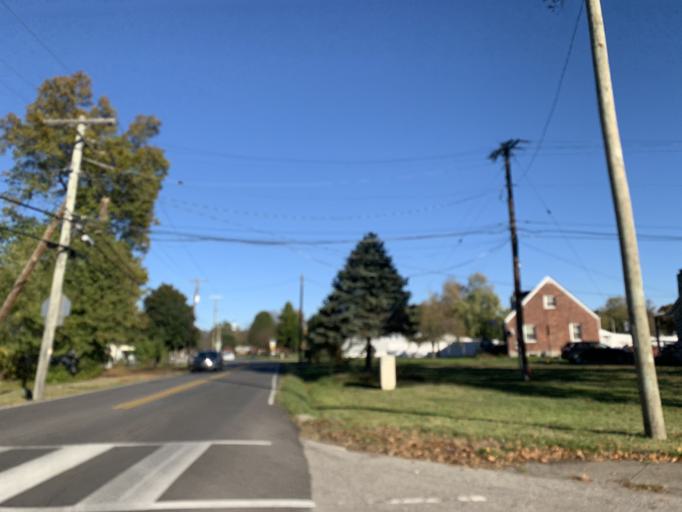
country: US
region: Kentucky
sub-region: Jefferson County
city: Saint Dennis
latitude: 38.1673
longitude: -85.8380
